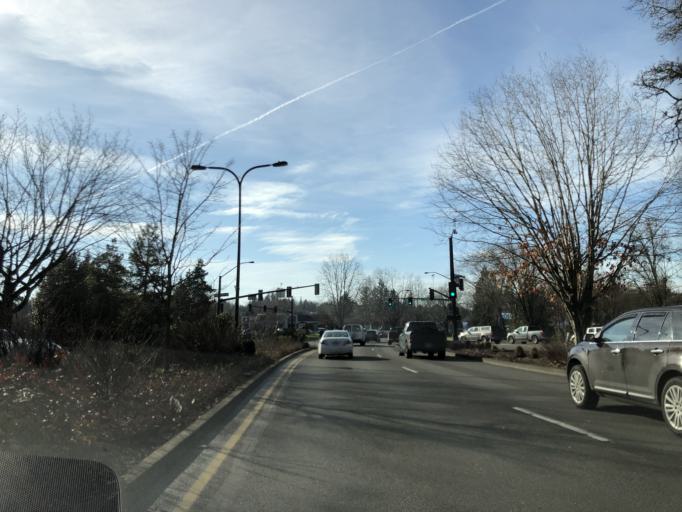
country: US
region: Oregon
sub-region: Washington County
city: Tualatin
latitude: 45.3821
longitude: -122.7581
